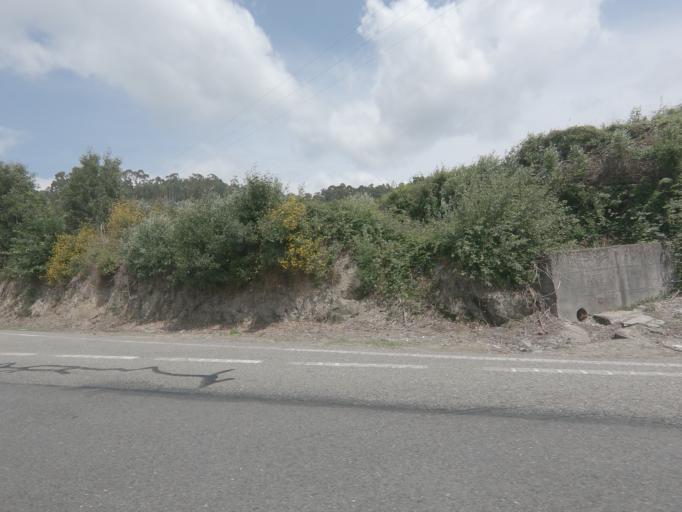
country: ES
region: Galicia
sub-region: Provincia de Pontevedra
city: Tomino
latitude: 42.0381
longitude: -8.7279
